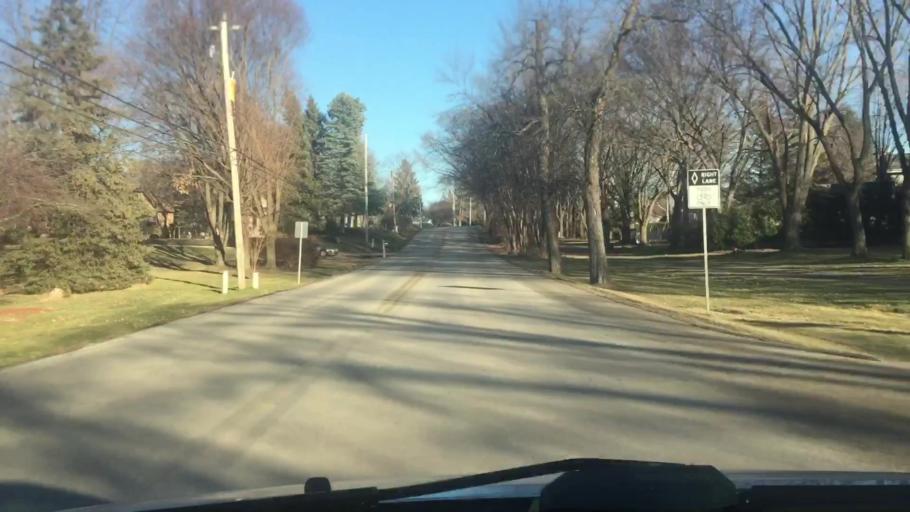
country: US
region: Wisconsin
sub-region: Waukesha County
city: Waukesha
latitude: 43.0584
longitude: -88.1807
